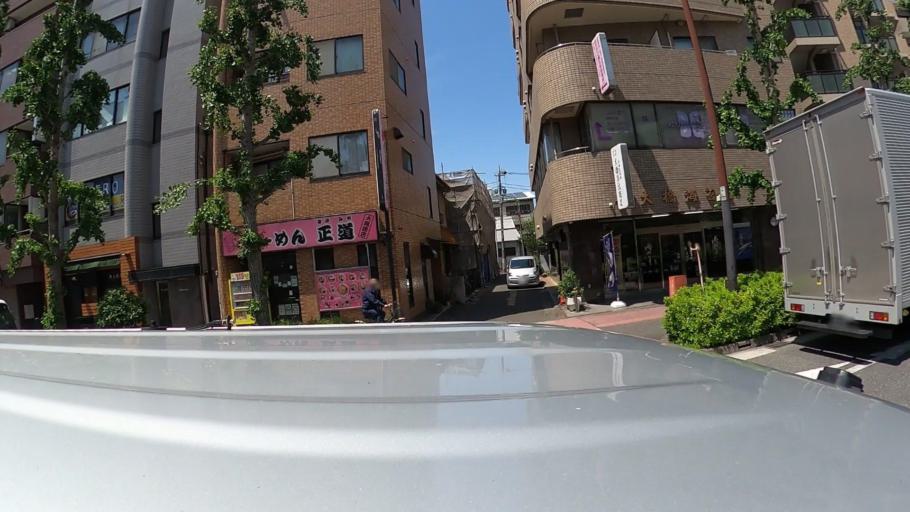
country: JP
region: Kanagawa
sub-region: Kawasaki-shi
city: Kawasaki
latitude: 35.5534
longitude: 139.7400
